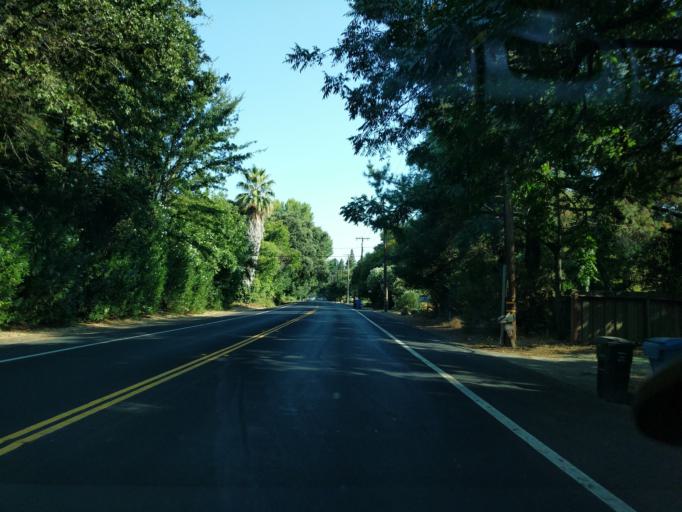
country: US
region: California
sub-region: Contra Costa County
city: Alamo
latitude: 37.8685
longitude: -122.0440
